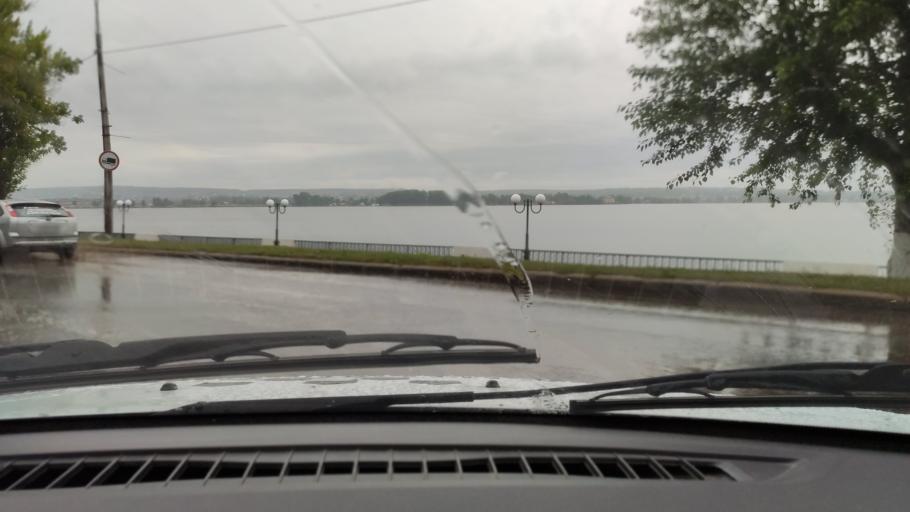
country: RU
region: Udmurtiya
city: Votkinsk
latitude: 57.0616
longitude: 53.9871
